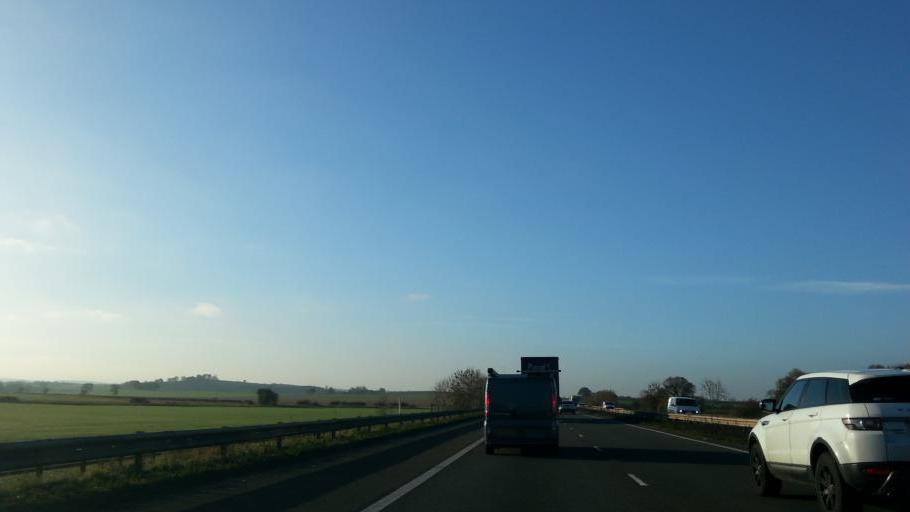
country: GB
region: England
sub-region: Derbyshire
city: Netherseal
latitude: 52.6509
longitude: -1.5900
